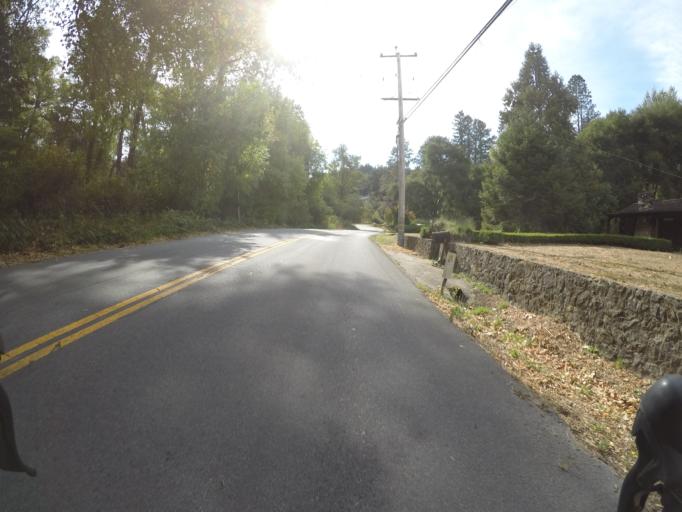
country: US
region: California
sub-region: Santa Cruz County
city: Mount Hermon
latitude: 37.0610
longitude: -122.0575
